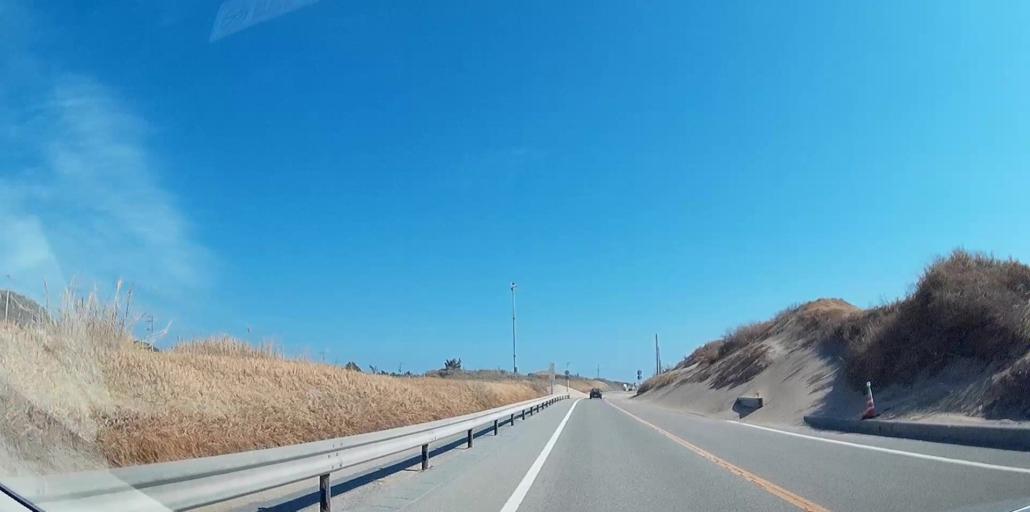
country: JP
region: Chiba
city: Tateyama
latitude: 34.9071
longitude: 139.8361
